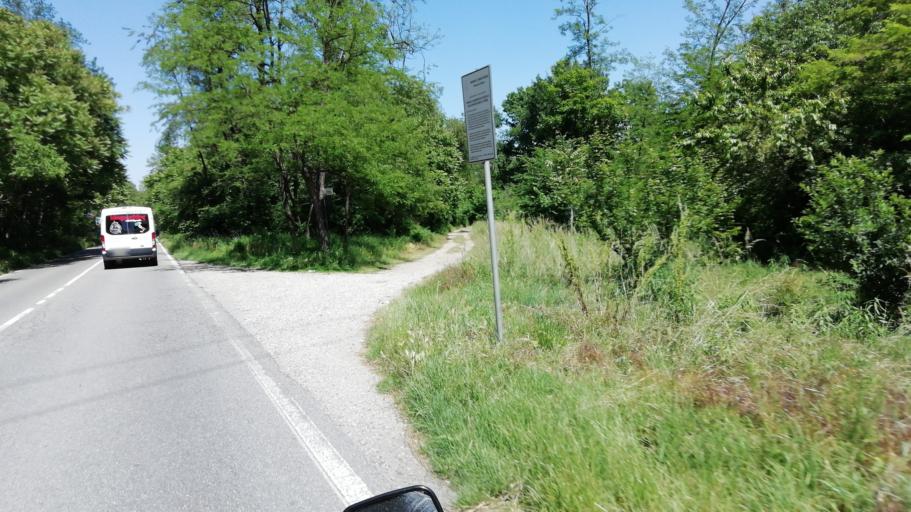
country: IT
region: Lombardy
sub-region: Provincia di Varese
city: Lonate Pozzolo
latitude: 45.5871
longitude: 8.7299
